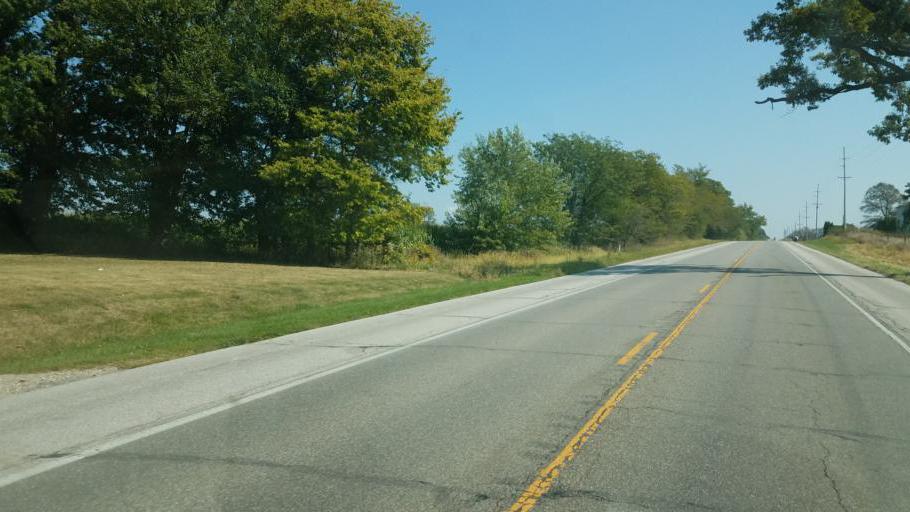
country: US
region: Indiana
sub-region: LaGrange County
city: Lagrange
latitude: 41.6418
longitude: -85.3677
